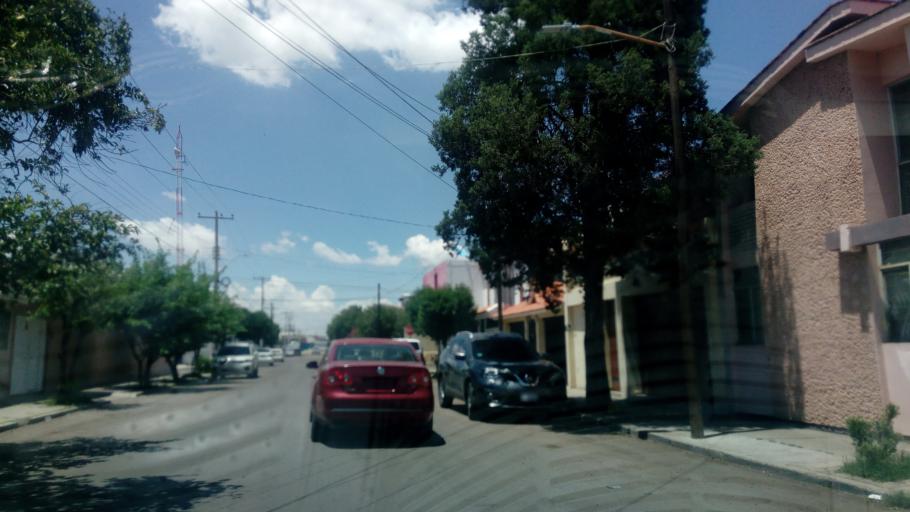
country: MX
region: Durango
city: Victoria de Durango
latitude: 24.0308
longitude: -104.6360
